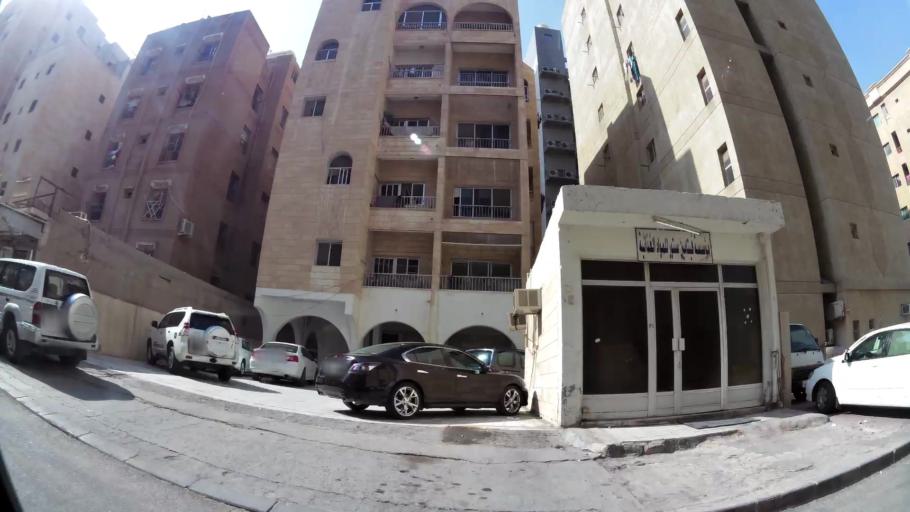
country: KW
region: Muhafazat Hawalli
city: Hawalli
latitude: 29.3359
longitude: 48.0325
